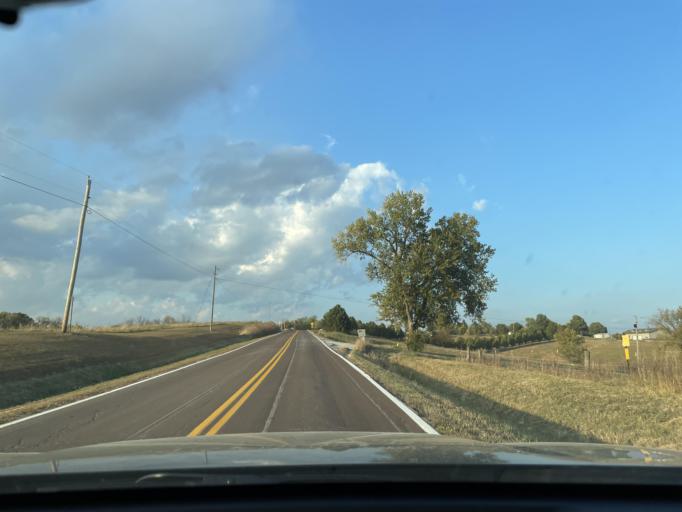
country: US
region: Missouri
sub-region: Andrew County
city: Savannah
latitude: 39.9118
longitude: -94.8767
